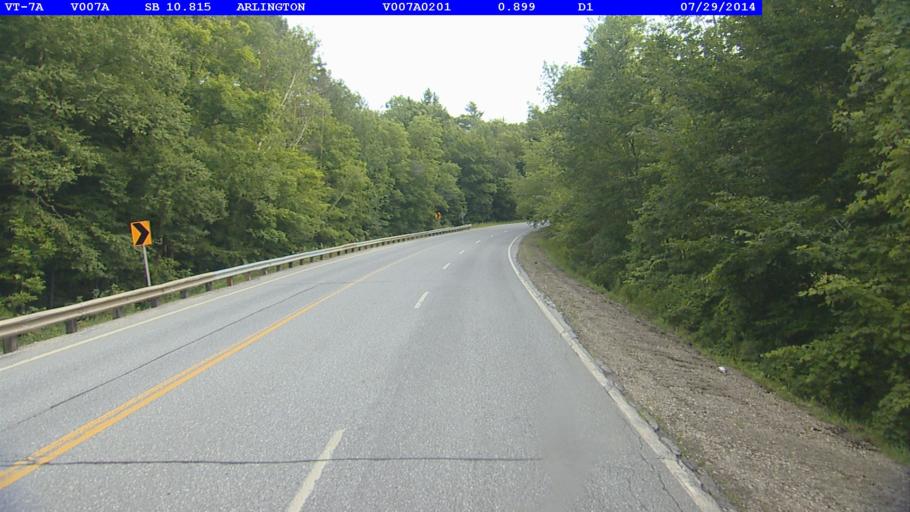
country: US
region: Vermont
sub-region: Bennington County
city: Arlington
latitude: 43.0368
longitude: -73.1762
